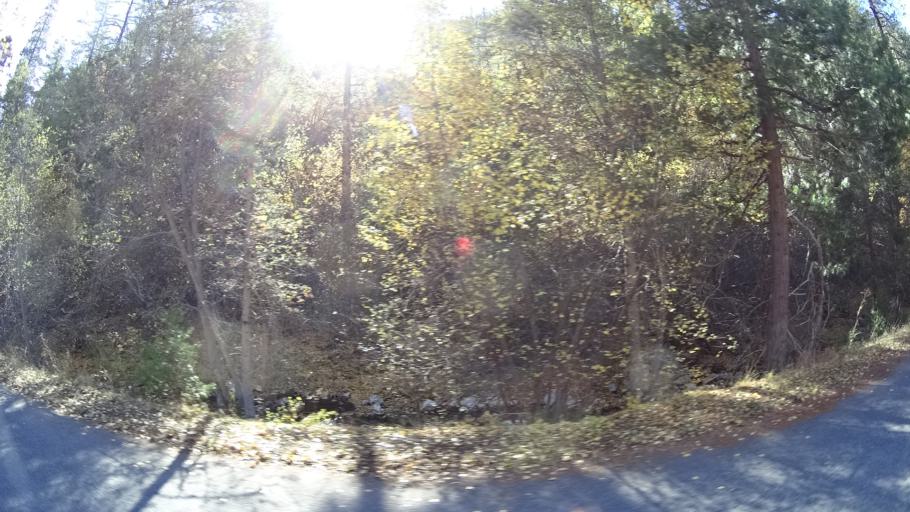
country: US
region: California
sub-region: Siskiyou County
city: Yreka
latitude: 41.6322
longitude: -122.7346
